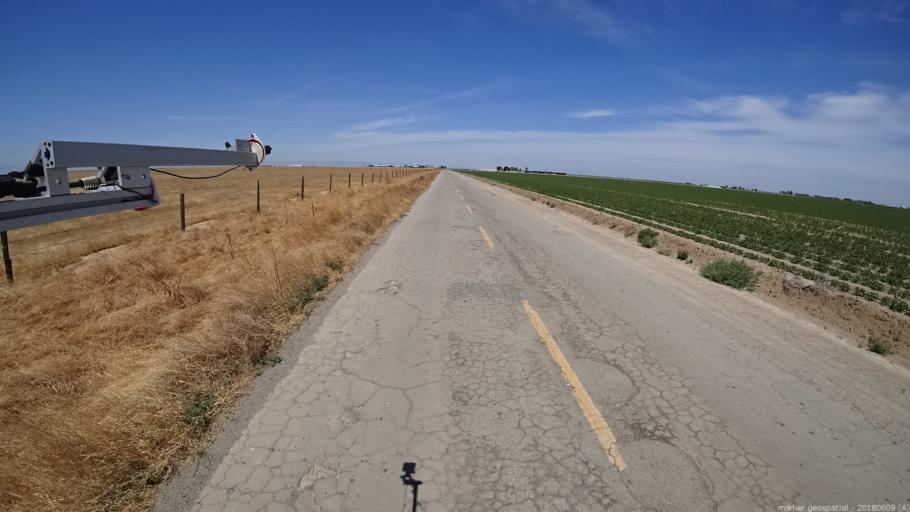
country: US
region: California
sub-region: Madera County
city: Fairmead
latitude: 36.9383
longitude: -120.2759
